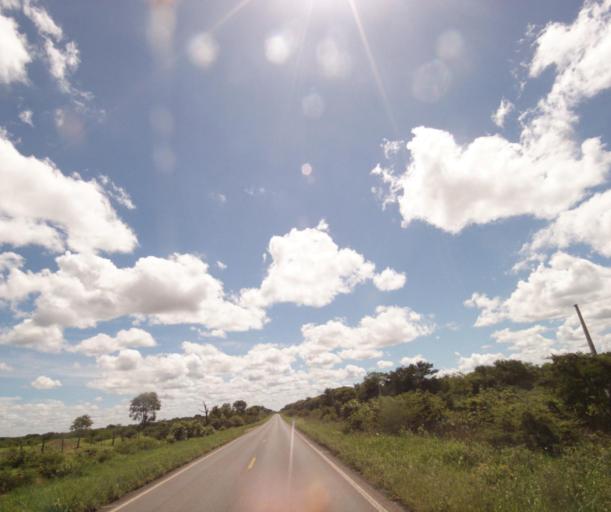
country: BR
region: Bahia
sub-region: Sao Felix Do Coribe
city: Santa Maria da Vitoria
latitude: -13.3912
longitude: -44.1123
